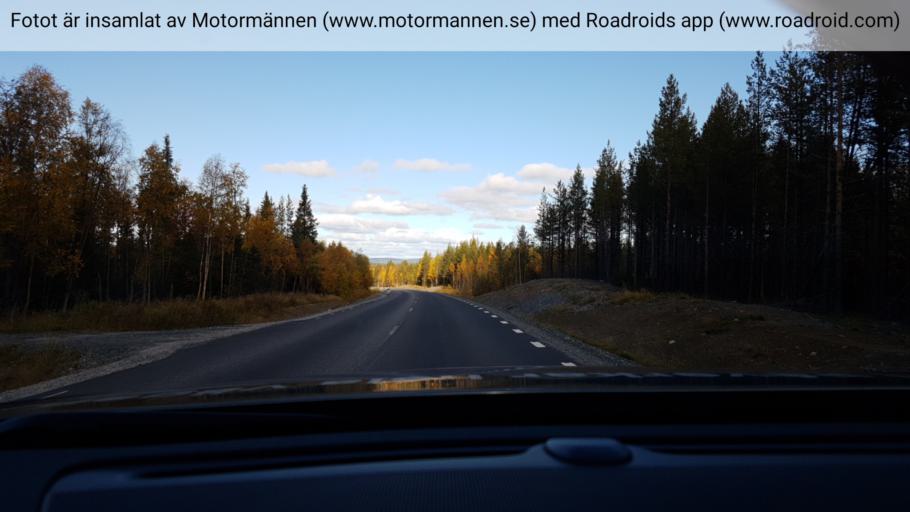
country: SE
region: Norrbotten
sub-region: Gallivare Kommun
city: Gaellivare
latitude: 67.0740
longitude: 20.7515
